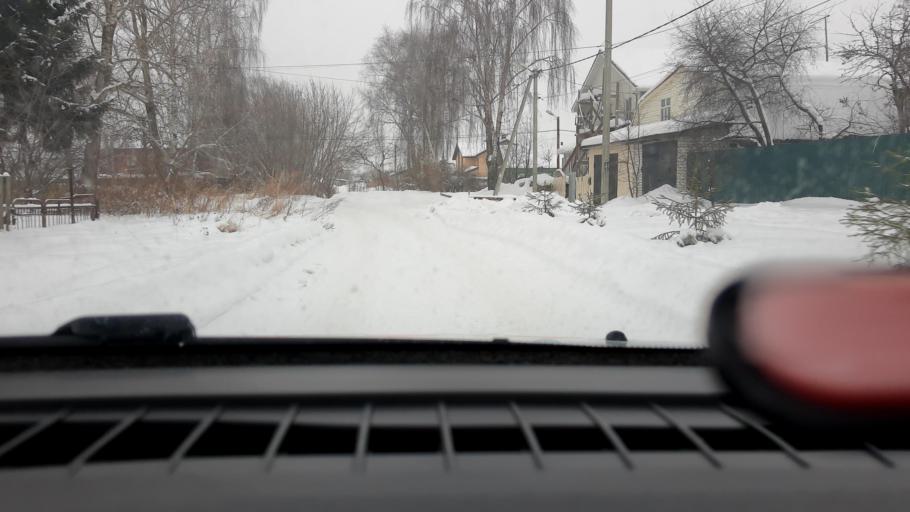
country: RU
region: Nizjnij Novgorod
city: Kstovo
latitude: 56.1903
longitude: 44.1577
